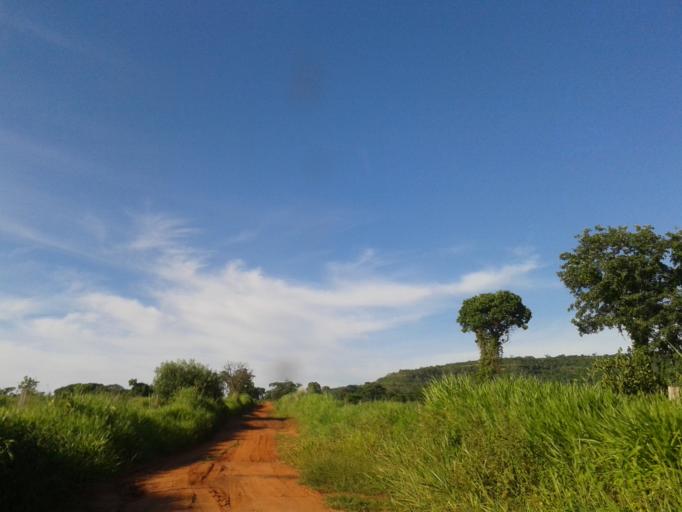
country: BR
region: Minas Gerais
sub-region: Santa Vitoria
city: Santa Vitoria
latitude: -19.0848
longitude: -49.9621
